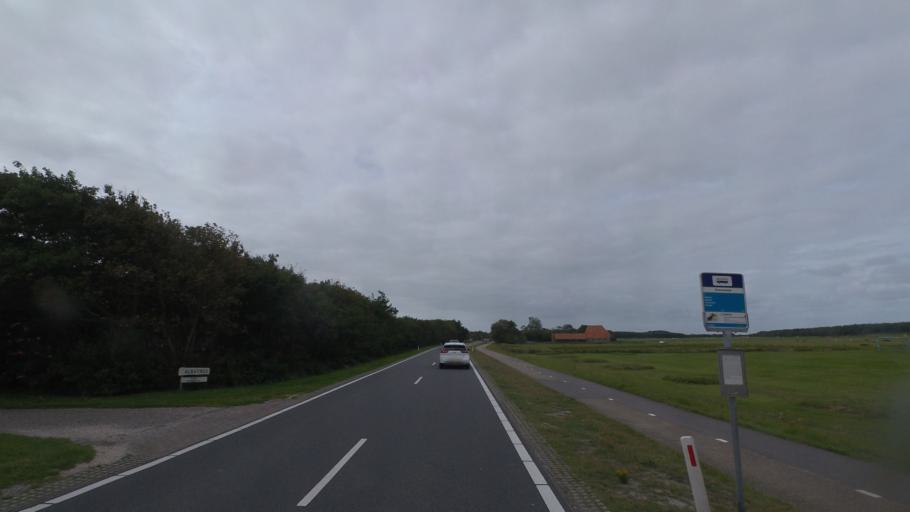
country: NL
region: Friesland
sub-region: Gemeente Ameland
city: Nes
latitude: 53.4454
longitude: 5.7261
